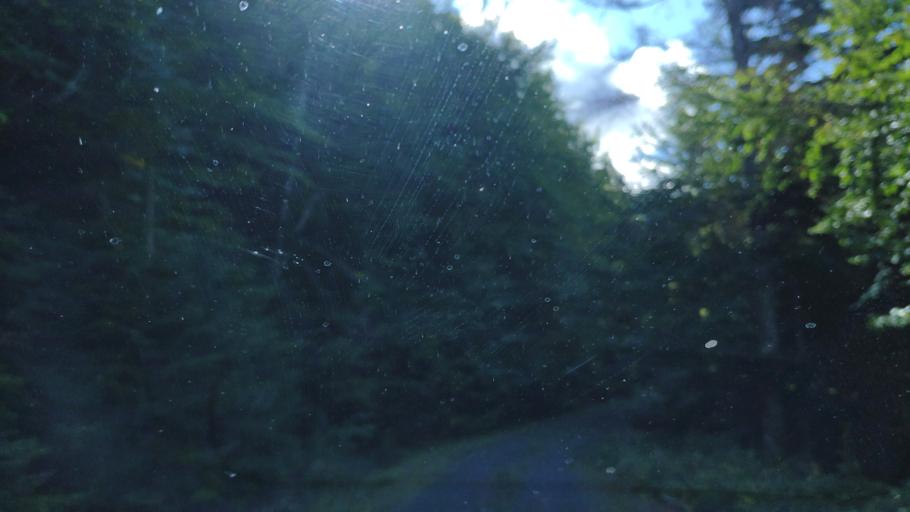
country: GR
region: Epirus
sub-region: Nomos Ioanninon
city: Metsovo
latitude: 39.8909
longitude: 21.2162
